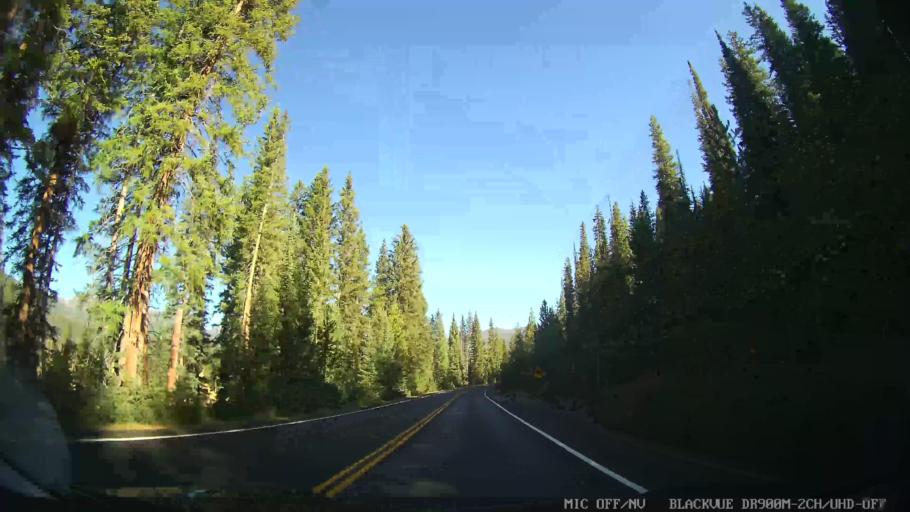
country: US
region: Colorado
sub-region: Grand County
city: Granby
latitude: 40.3036
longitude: -105.8427
